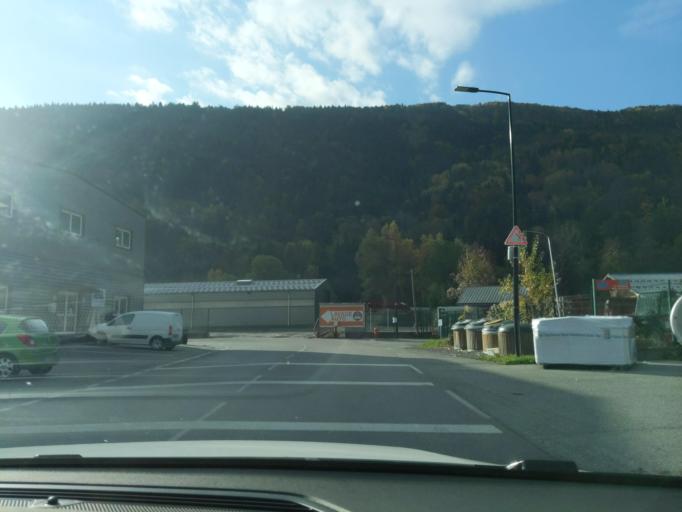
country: FR
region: Rhone-Alpes
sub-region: Departement de la Savoie
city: Aime
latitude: 45.5511
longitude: 6.6417
